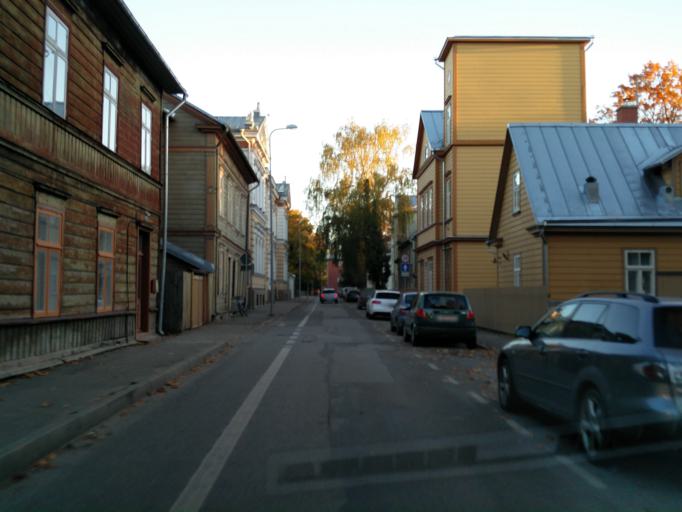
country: EE
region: Tartu
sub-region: Tartu linn
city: Tartu
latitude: 58.3784
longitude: 26.7106
